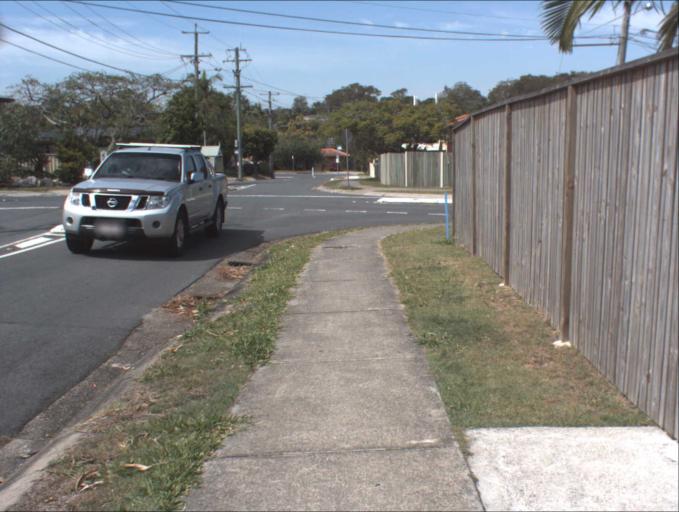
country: AU
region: Queensland
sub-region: Logan
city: Rochedale South
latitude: -27.5948
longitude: 153.1259
